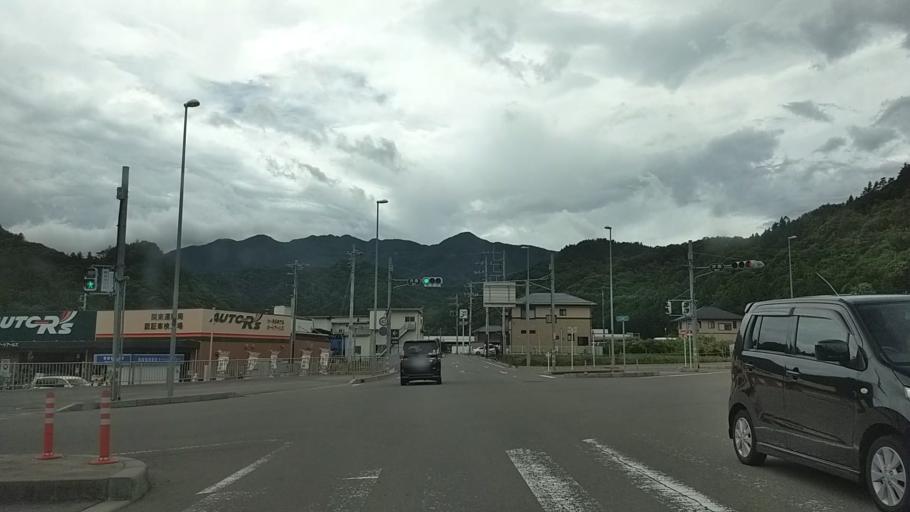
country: JP
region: Yamanashi
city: Otsuki
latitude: 35.5708
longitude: 138.9314
